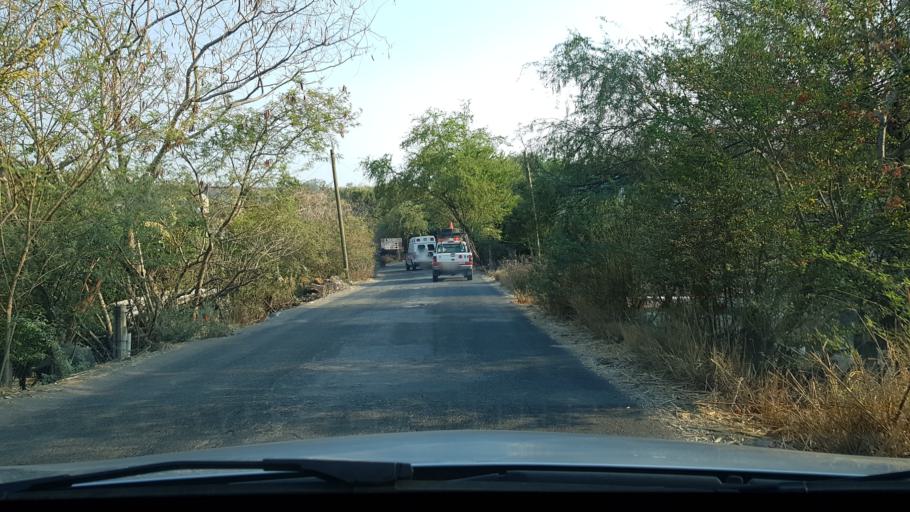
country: MX
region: Morelos
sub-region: Tepalcingo
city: Zacapalco
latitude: 18.6371
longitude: -99.0082
